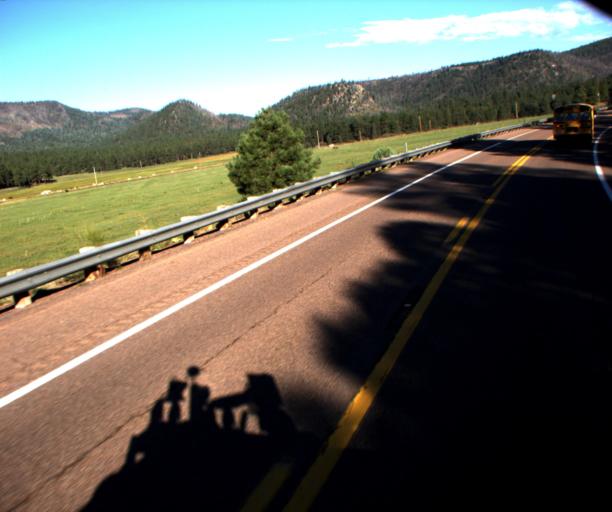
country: US
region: Arizona
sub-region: Apache County
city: Eagar
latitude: 33.8583
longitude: -109.1603
